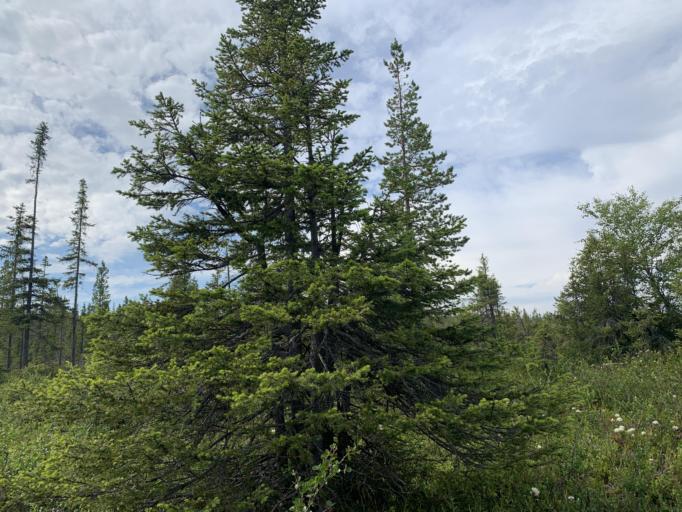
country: RU
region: Murmansk
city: Monchegorsk
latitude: 67.7982
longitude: 33.1168
